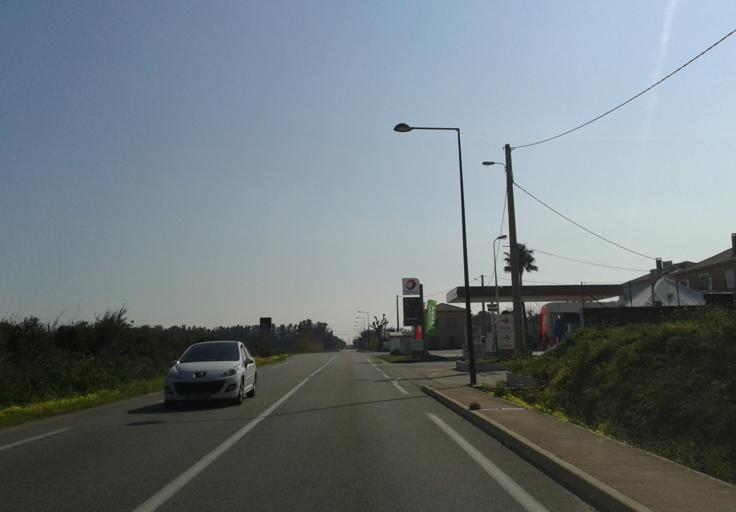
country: FR
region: Corsica
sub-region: Departement de la Haute-Corse
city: Linguizzetta
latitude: 42.2600
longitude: 9.5474
